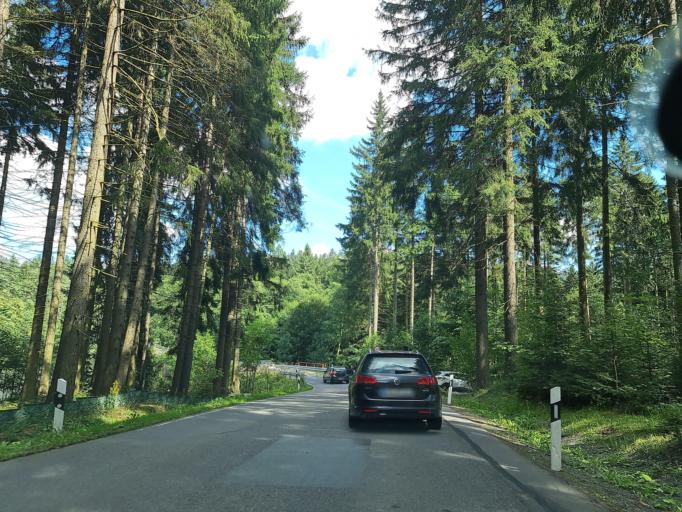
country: DE
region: Saxony
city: Elterlein
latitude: 50.5918
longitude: 12.8895
